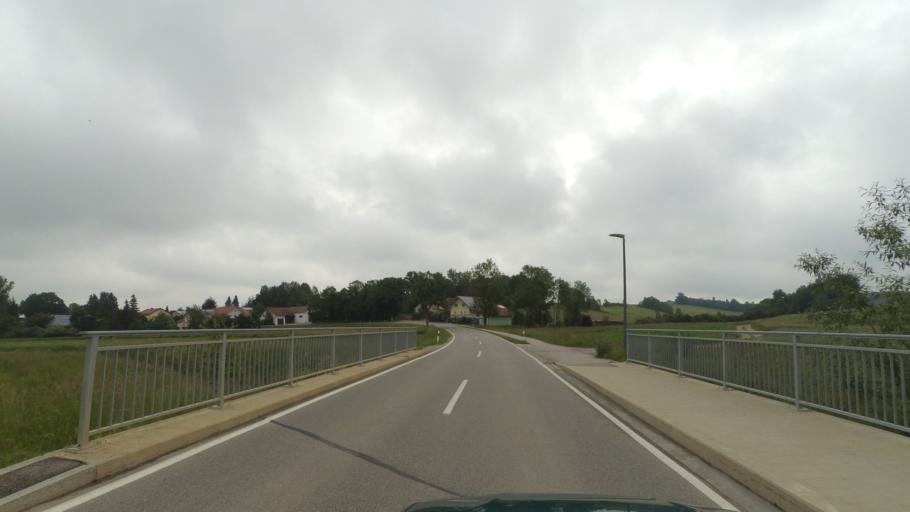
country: DE
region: Bavaria
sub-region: Lower Bavaria
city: Geiselhoring
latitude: 48.8001
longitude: 12.3805
